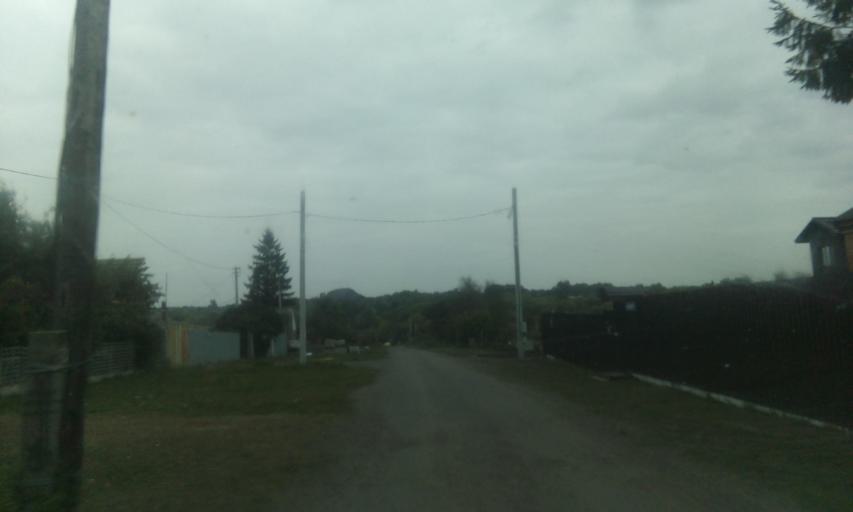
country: RU
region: Tula
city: Dubovka
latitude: 53.9466
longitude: 38.0230
